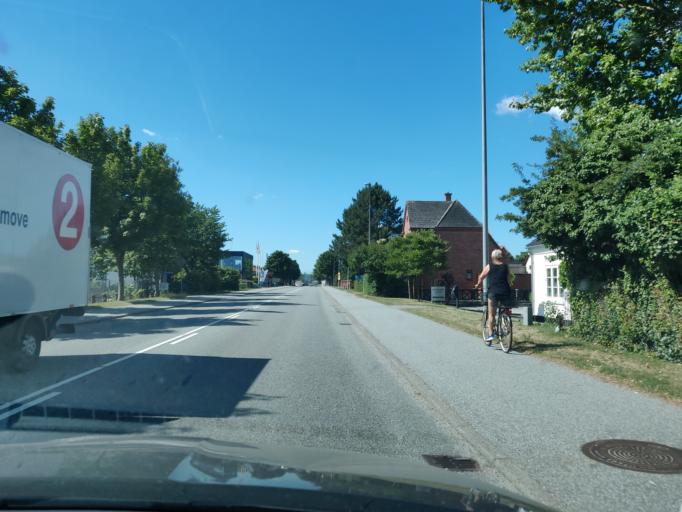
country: DK
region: North Denmark
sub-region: Alborg Kommune
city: Aalborg
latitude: 57.0781
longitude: 9.9551
